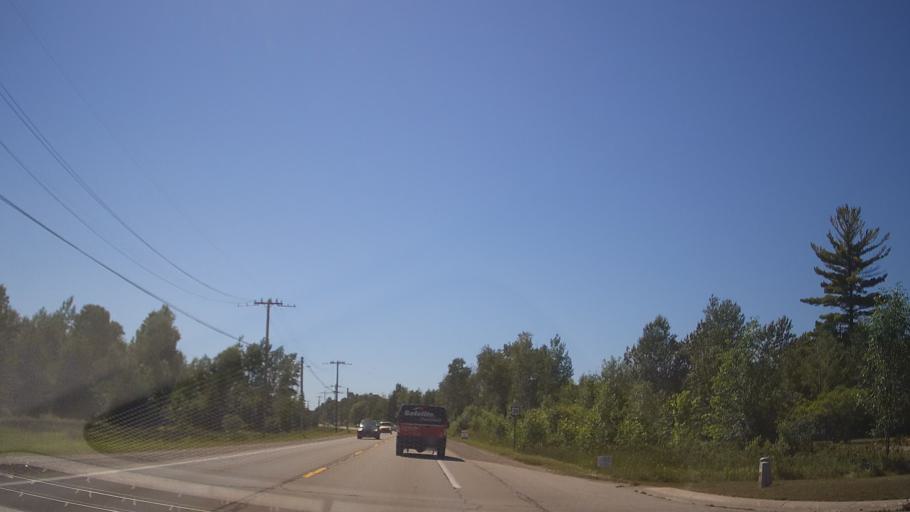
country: US
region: Michigan
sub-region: Emmet County
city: Petoskey
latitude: 45.4243
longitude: -84.8460
